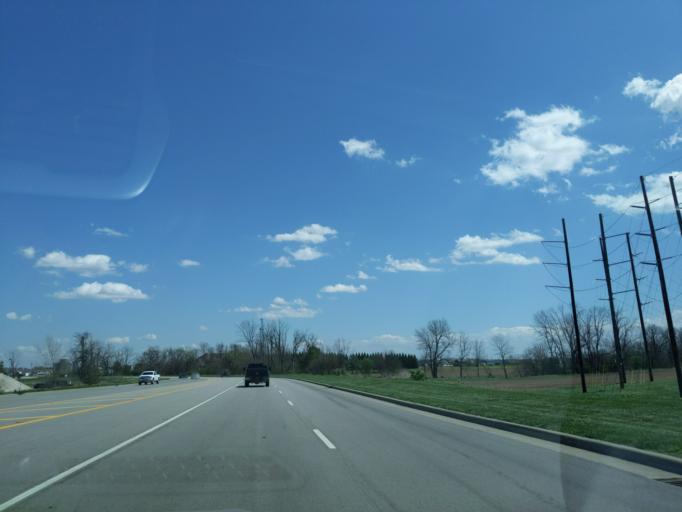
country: US
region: Indiana
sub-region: Decatur County
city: Greensburg
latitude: 39.3590
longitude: -85.5163
